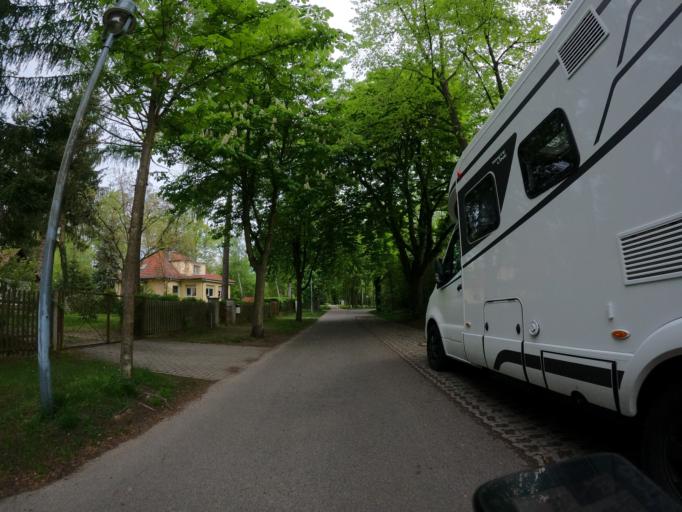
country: DE
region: Brandenburg
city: Konigs Wusterhausen
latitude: 52.2965
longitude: 13.6608
